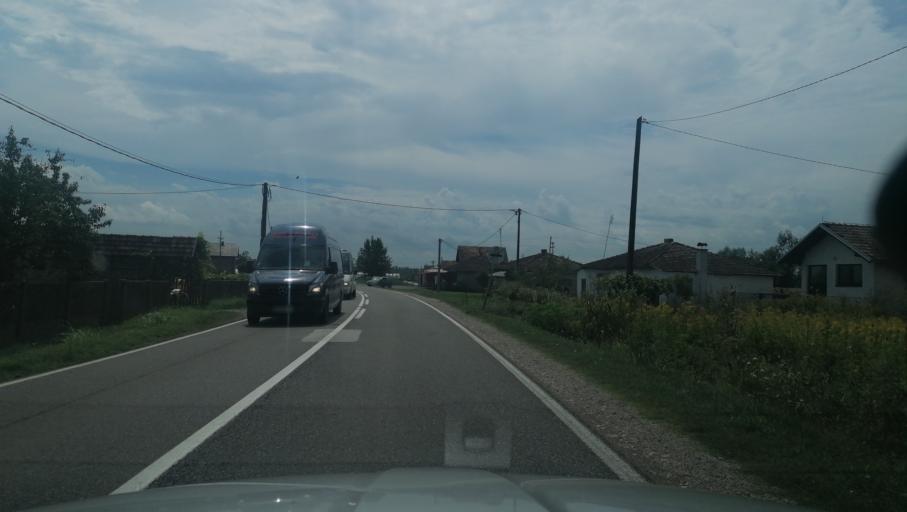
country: BA
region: Republika Srpska
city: Bosanski Samac
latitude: 45.0195
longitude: 18.5173
